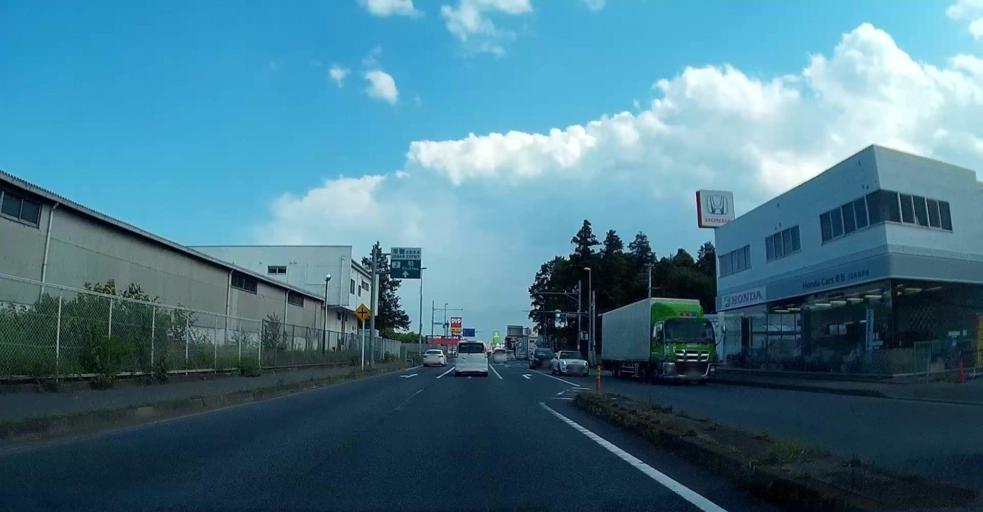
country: JP
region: Chiba
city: Noda
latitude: 35.9459
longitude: 139.8837
